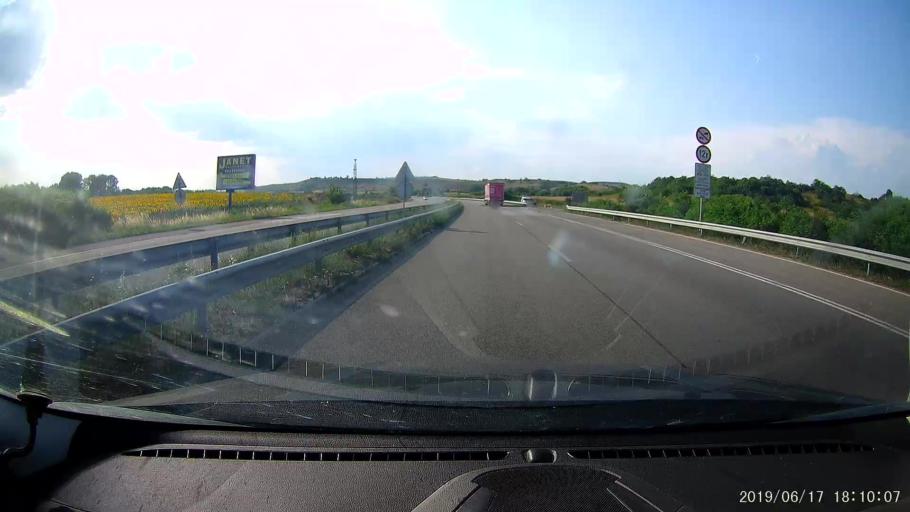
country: BG
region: Khaskovo
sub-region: Obshtina Lyubimets
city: Lyubimets
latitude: 41.8705
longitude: 26.0828
